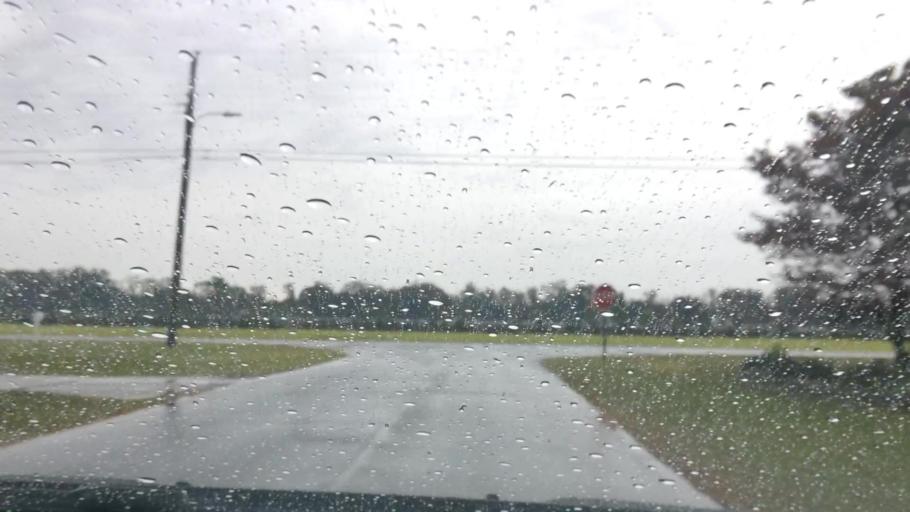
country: US
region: North Carolina
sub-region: Pitt County
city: Grifton
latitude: 35.3824
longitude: -77.4169
